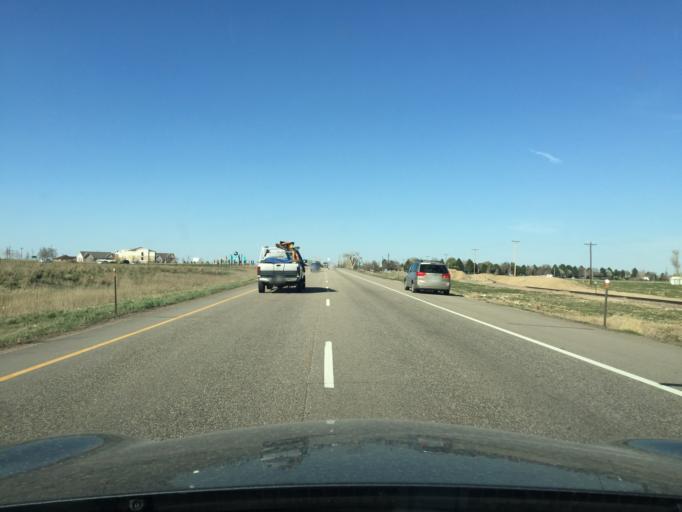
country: US
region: Colorado
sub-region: Boulder County
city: Longmont
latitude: 40.1351
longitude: -105.1352
